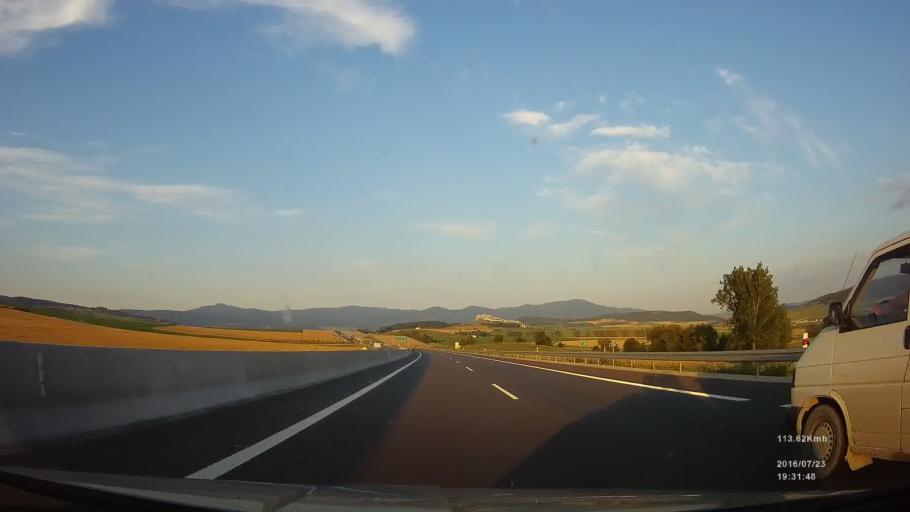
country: SK
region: Presovsky
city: Spisske Podhradie
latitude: 49.0063
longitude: 20.6909
